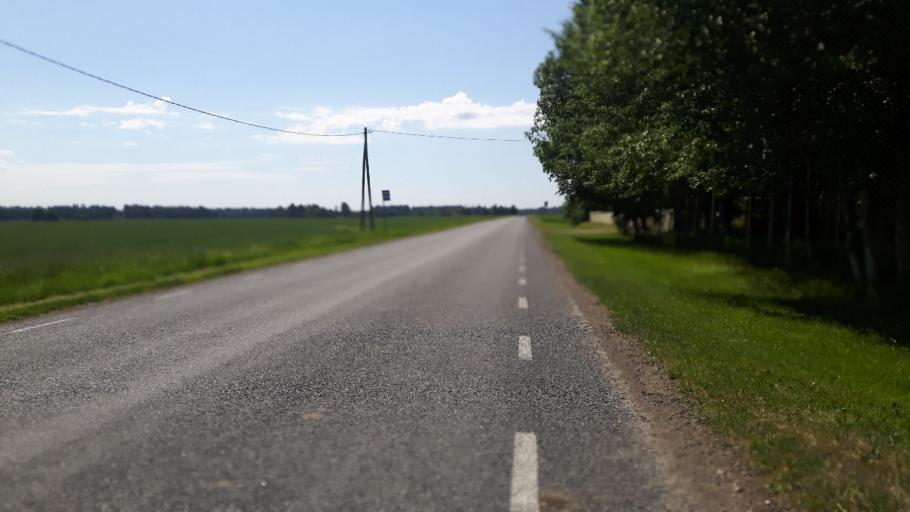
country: EE
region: Paernumaa
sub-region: Vaendra vald (alev)
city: Vandra
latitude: 58.6210
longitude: 25.0211
